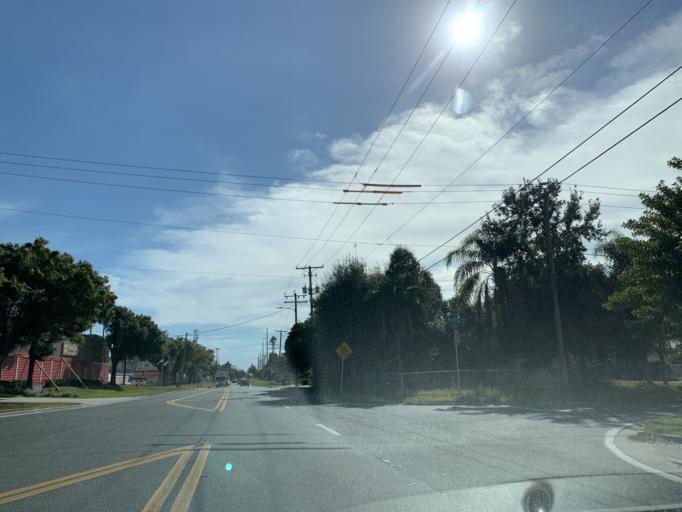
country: US
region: Florida
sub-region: Hillsborough County
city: Tampa
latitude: 27.8925
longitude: -82.5185
